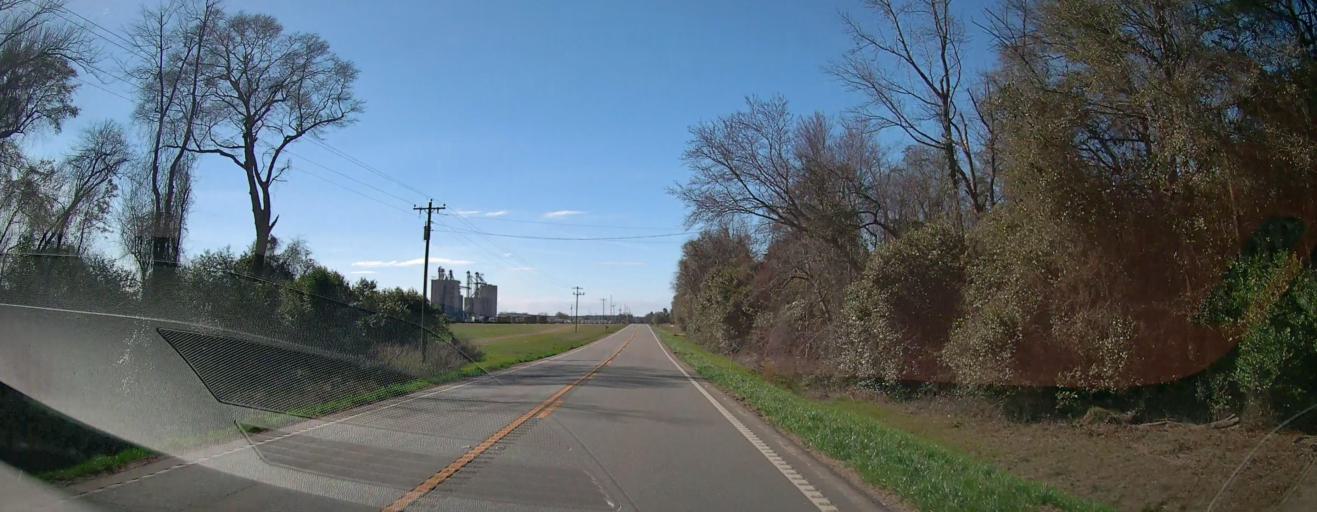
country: US
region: Georgia
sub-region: Macon County
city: Oglethorpe
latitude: 32.3327
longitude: -84.1050
